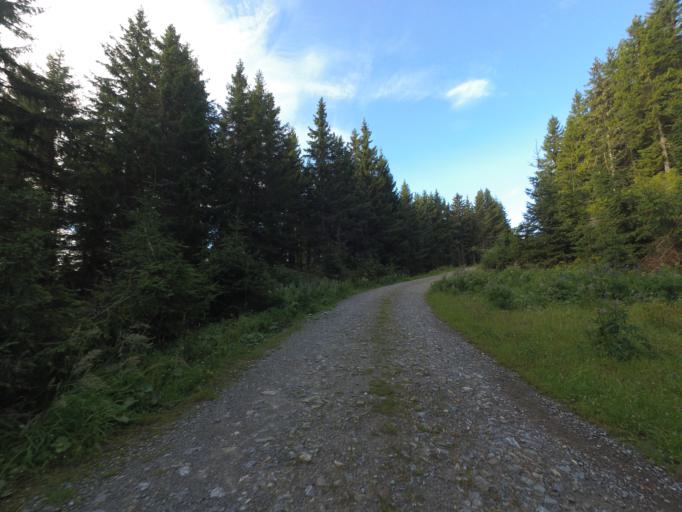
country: AT
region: Salzburg
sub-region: Politischer Bezirk Sankt Johann im Pongau
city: Goldegg
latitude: 47.3491
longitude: 13.0971
